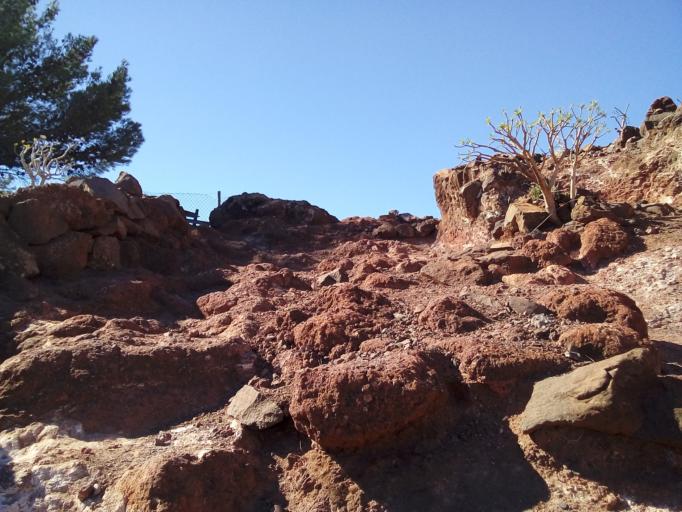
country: ES
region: Canary Islands
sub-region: Provincia de Santa Cruz de Tenerife
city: Vallehermosa
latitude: 28.1192
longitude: -17.3311
